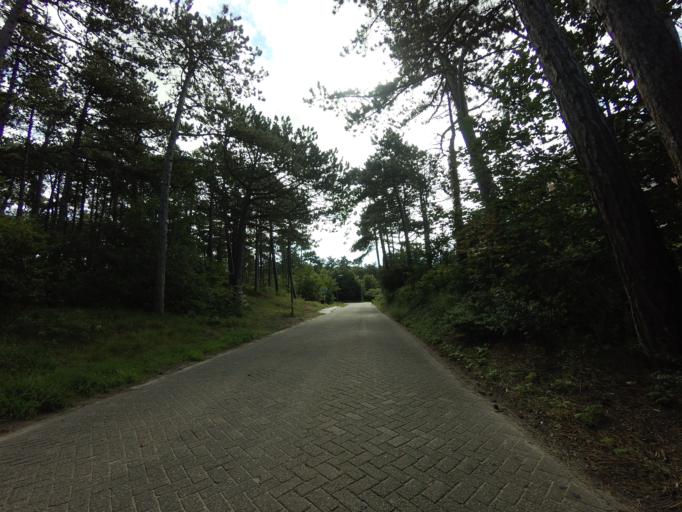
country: NL
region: Friesland
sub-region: Gemeente Terschelling
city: West-Terschelling
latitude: 53.3678
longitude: 5.2199
